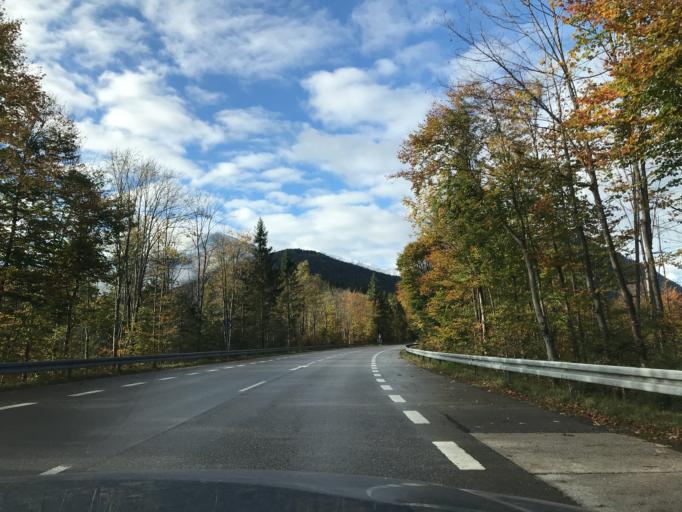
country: DE
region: Bavaria
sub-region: Upper Bavaria
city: Jachenau
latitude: 47.5745
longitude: 11.5365
